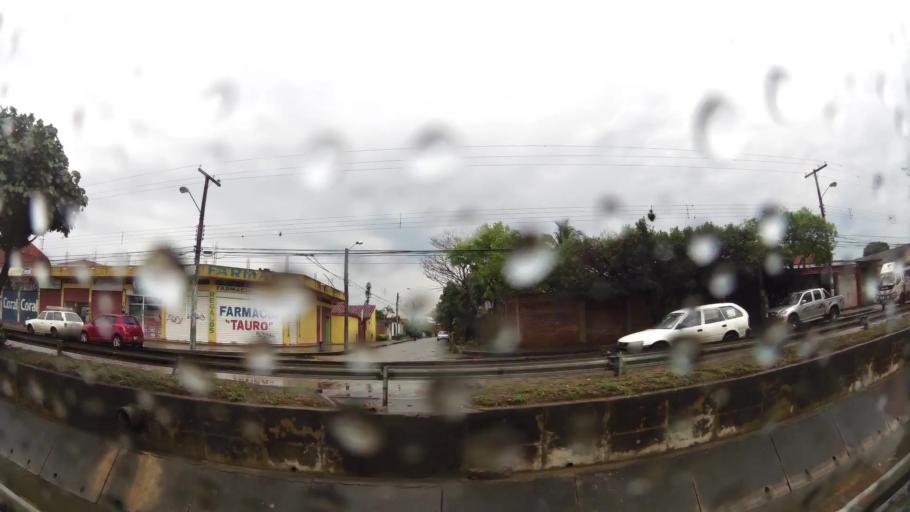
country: BO
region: Santa Cruz
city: Santa Cruz de la Sierra
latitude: -17.7967
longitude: -63.2109
